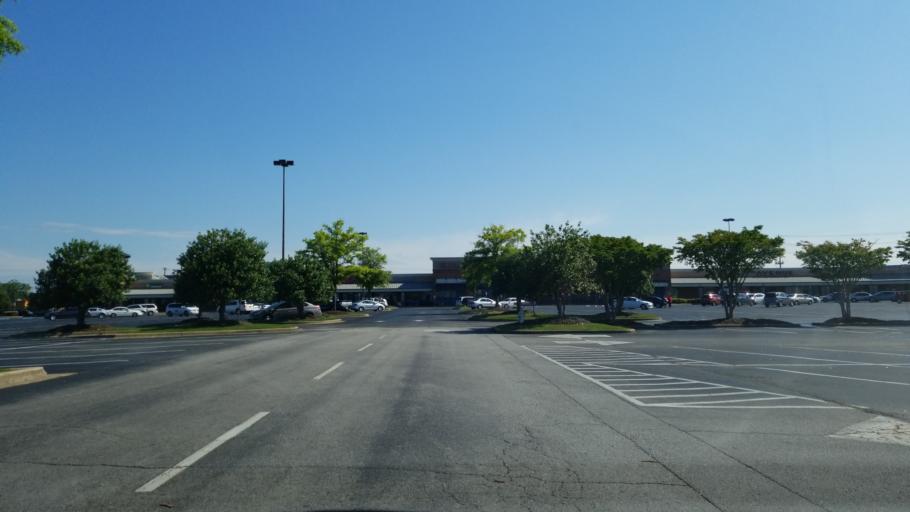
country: US
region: Tennessee
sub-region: Hamilton County
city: East Brainerd
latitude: 35.0322
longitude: -85.1523
